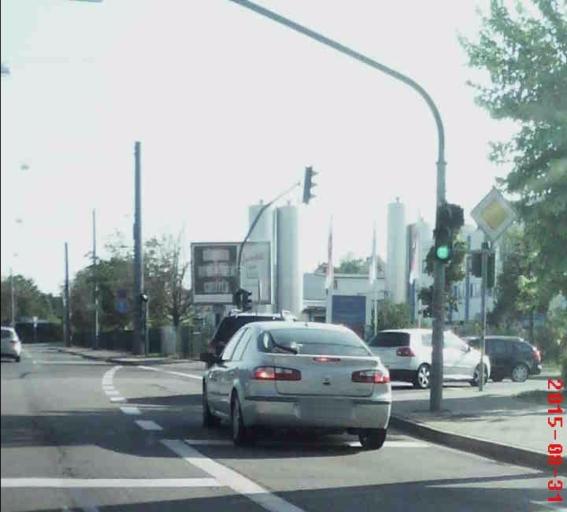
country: DE
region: Thuringia
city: Erfurt
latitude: 50.9887
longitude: 11.0542
